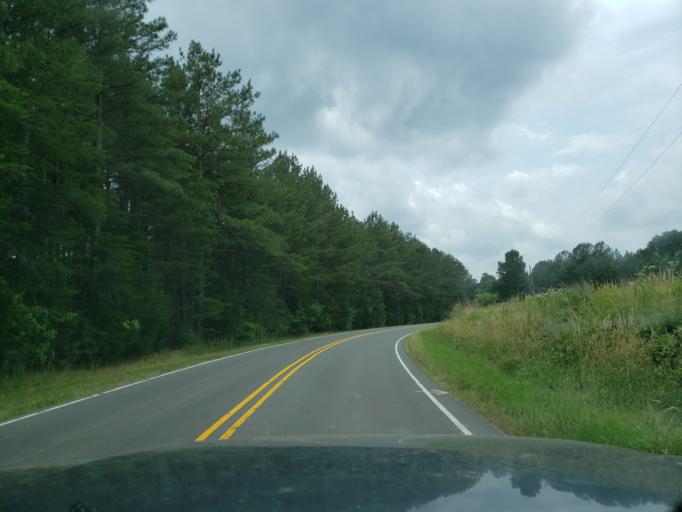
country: US
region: North Carolina
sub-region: Granville County
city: Butner
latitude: 36.1768
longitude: -78.8498
